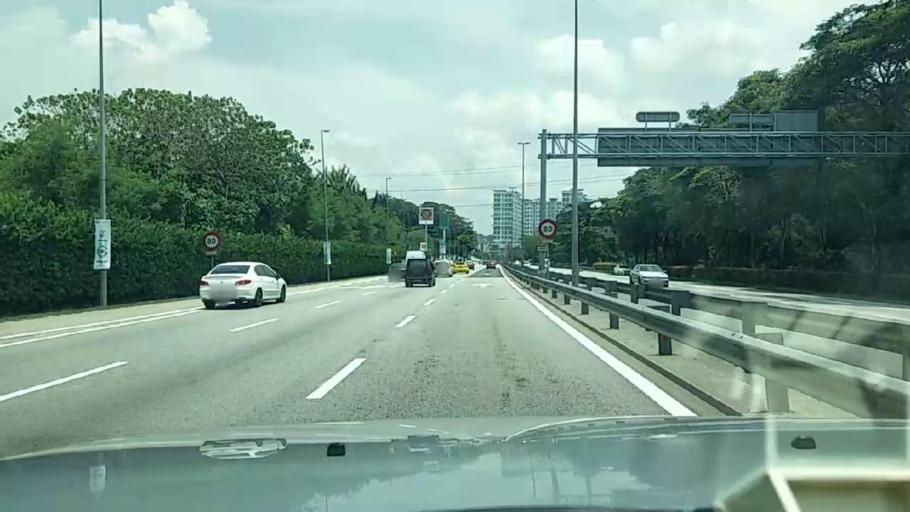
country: MY
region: Kuala Lumpur
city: Kuala Lumpur
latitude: 3.0941
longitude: 101.6833
